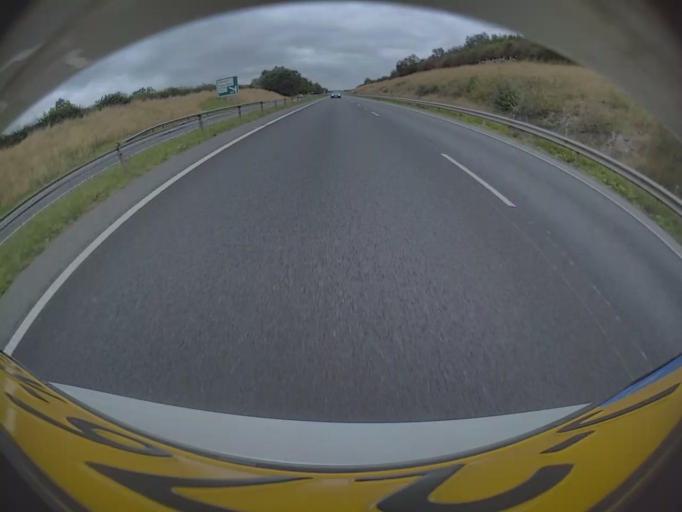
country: GB
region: Wales
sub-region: Anglesey
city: Llanfairpwllgwyngyll
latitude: 53.2242
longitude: -4.2384
